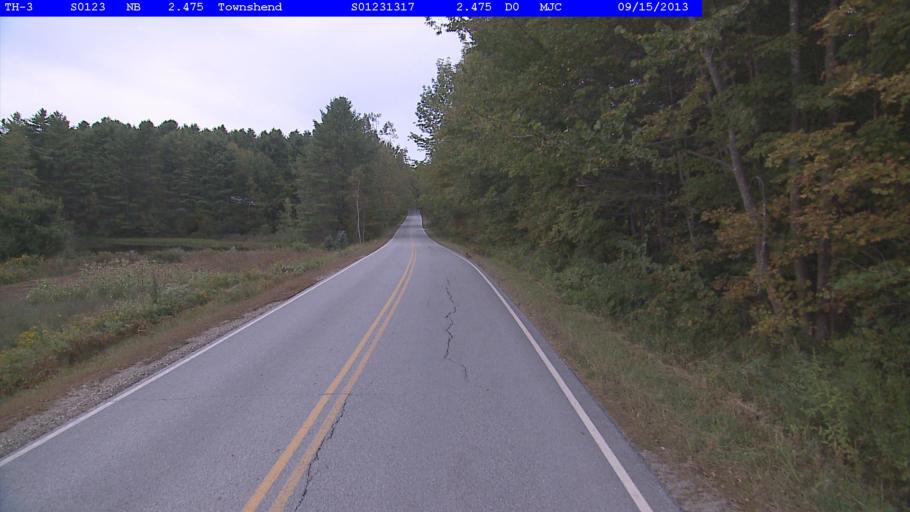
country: US
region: Vermont
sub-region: Windham County
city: Newfane
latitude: 43.1180
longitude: -72.7088
